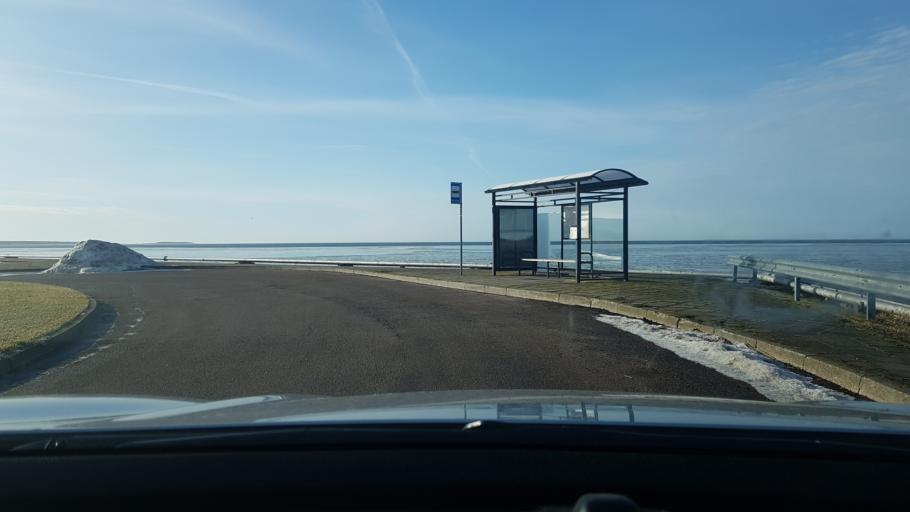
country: EE
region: Saare
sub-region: Kuressaare linn
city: Kuressaare
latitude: 58.2173
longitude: 22.5037
